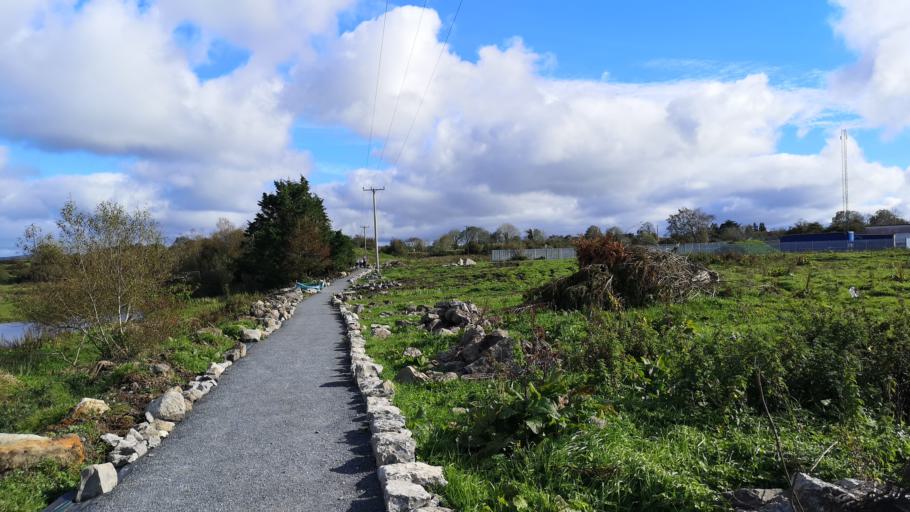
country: IE
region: Connaught
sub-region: County Galway
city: Gort
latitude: 53.0688
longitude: -8.8163
